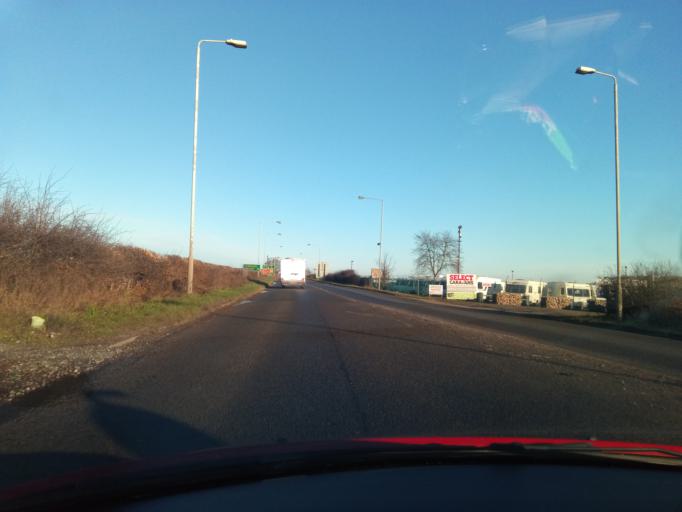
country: GB
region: England
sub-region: Nottinghamshire
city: Farnsfield
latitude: 53.0909
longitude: -1.0704
